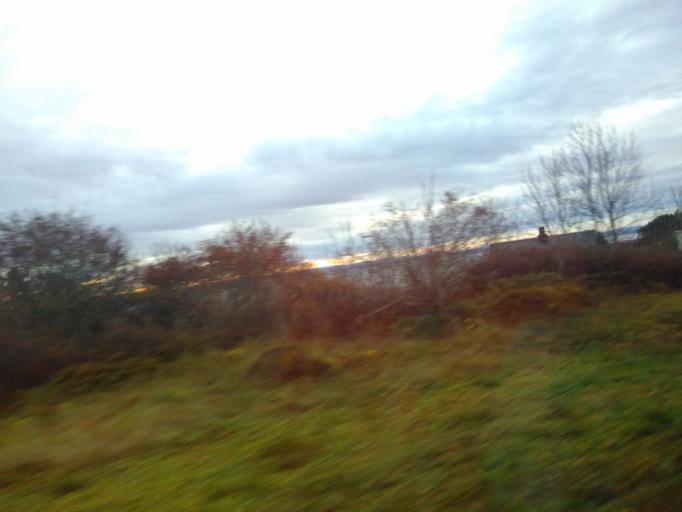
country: NO
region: Sor-Trondelag
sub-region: Froya
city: Sistranda
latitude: 63.7448
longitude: 8.8366
